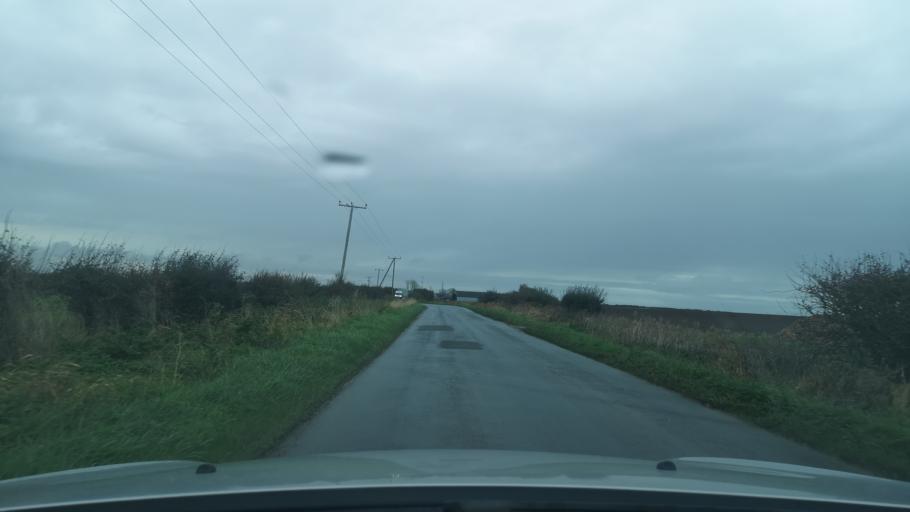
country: GB
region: England
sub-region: East Riding of Yorkshire
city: Easington
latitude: 53.6329
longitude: 0.1223
